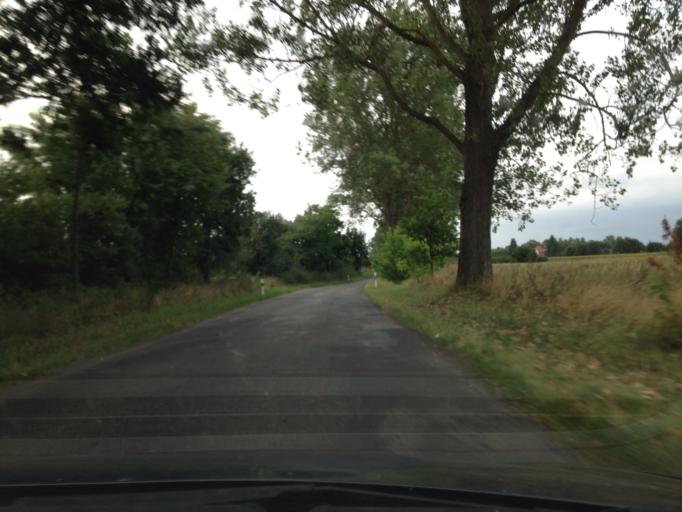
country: DE
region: Mecklenburg-Vorpommern
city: Loitz
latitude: 53.3091
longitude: 13.4196
